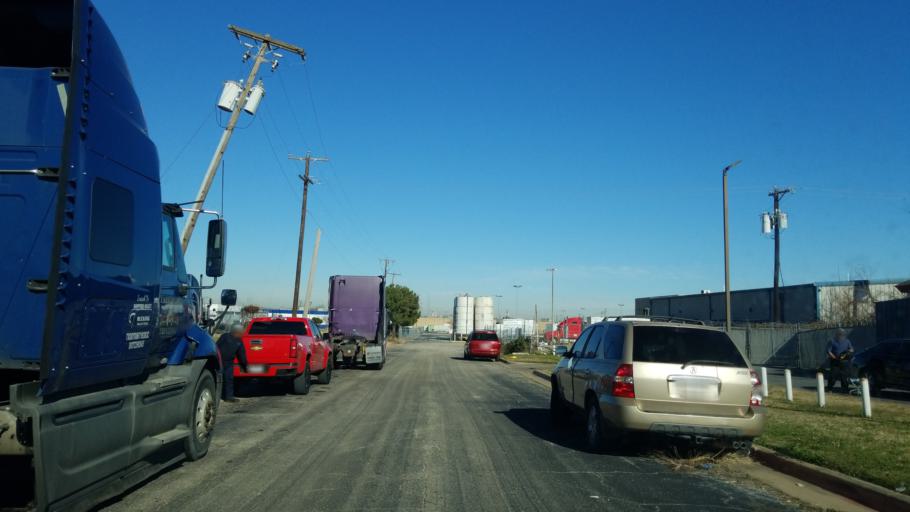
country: US
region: Texas
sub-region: Dallas County
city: Grand Prairie
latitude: 32.7407
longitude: -97.0508
